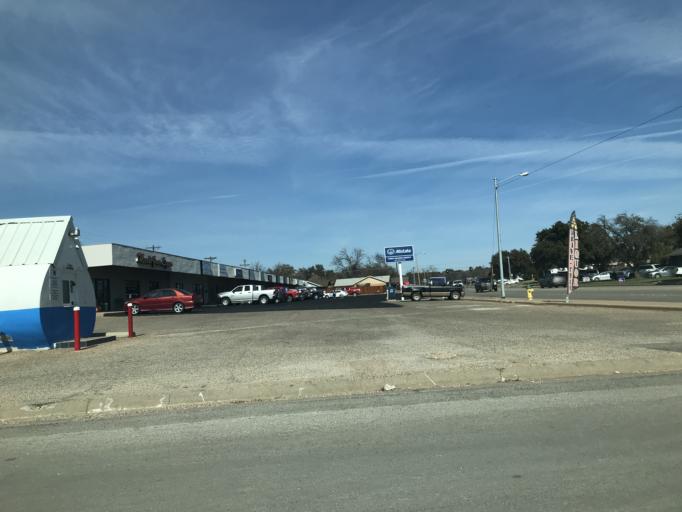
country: US
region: Texas
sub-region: Tom Green County
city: San Angelo
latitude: 31.4364
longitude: -100.4802
